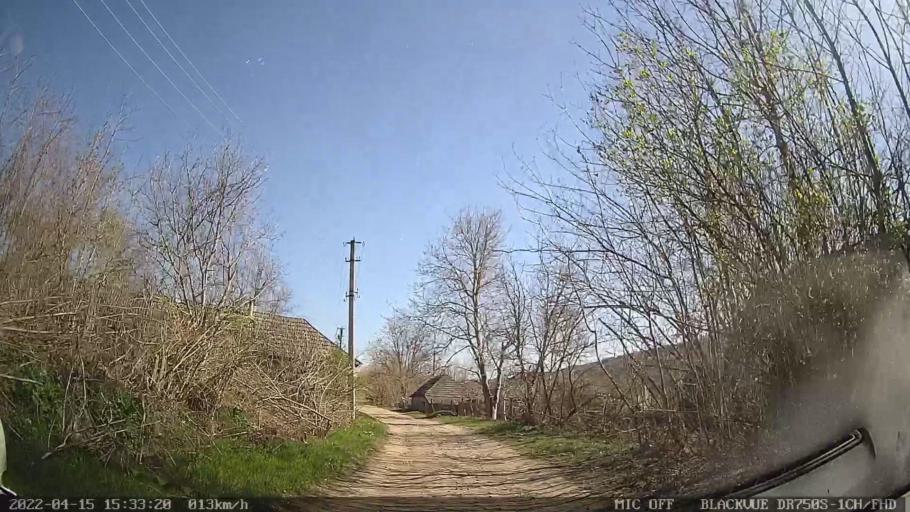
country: MD
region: Raionul Ocnita
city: Otaci
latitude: 48.3499
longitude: 27.9234
